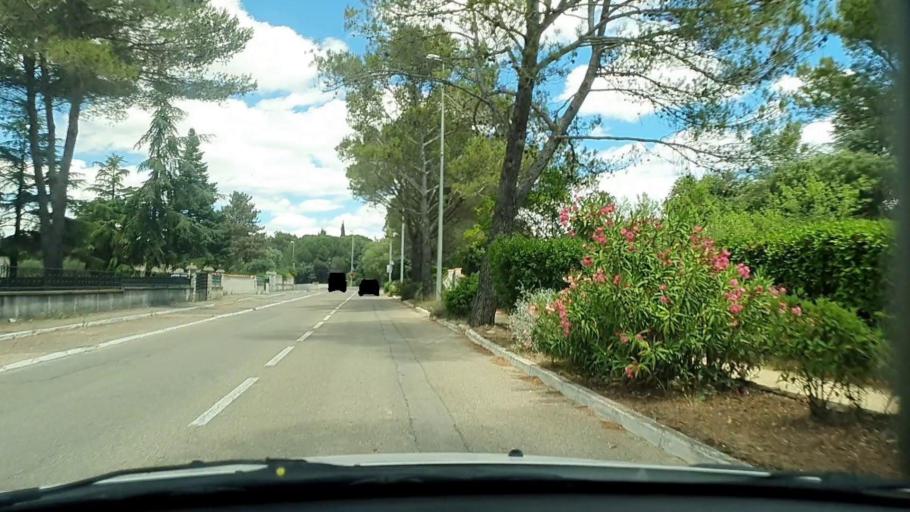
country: FR
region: Languedoc-Roussillon
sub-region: Departement du Gard
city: Poulx
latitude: 43.9048
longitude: 4.4214
